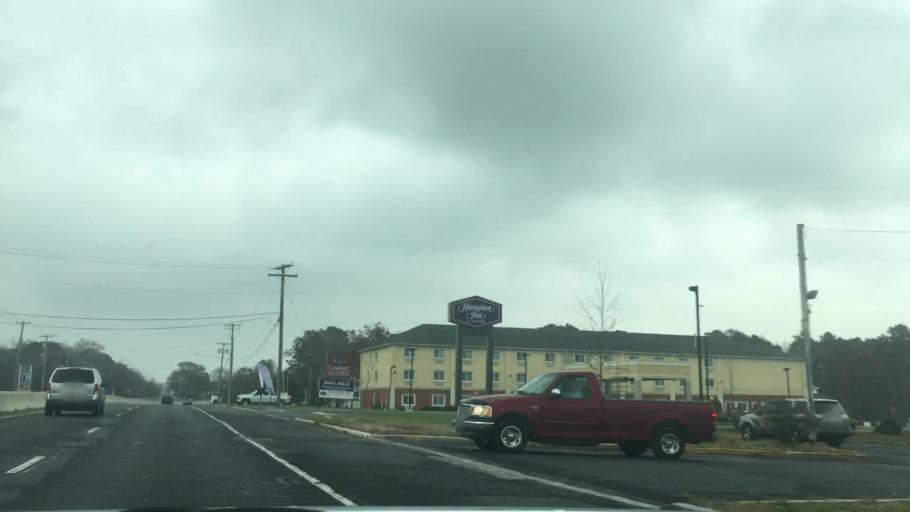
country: US
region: New Jersey
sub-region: Atlantic County
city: Absecon
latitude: 39.4407
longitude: -74.5207
